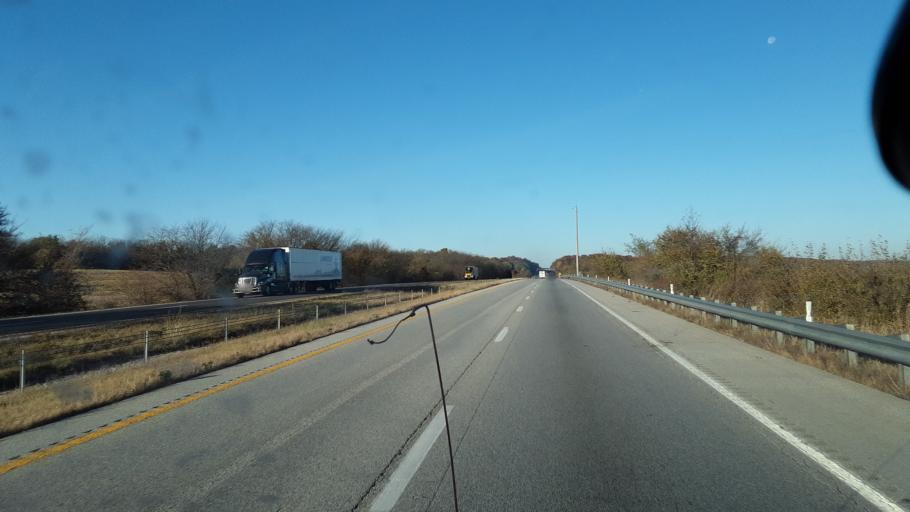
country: US
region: Missouri
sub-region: Cooper County
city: Boonville
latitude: 38.9340
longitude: -92.9315
